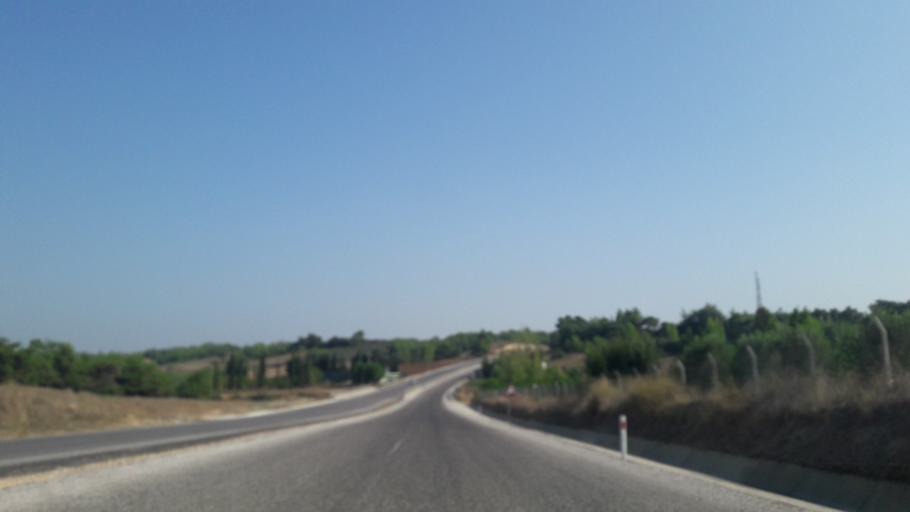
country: TR
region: Adana
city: Sagkaya
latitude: 37.1750
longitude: 35.5652
